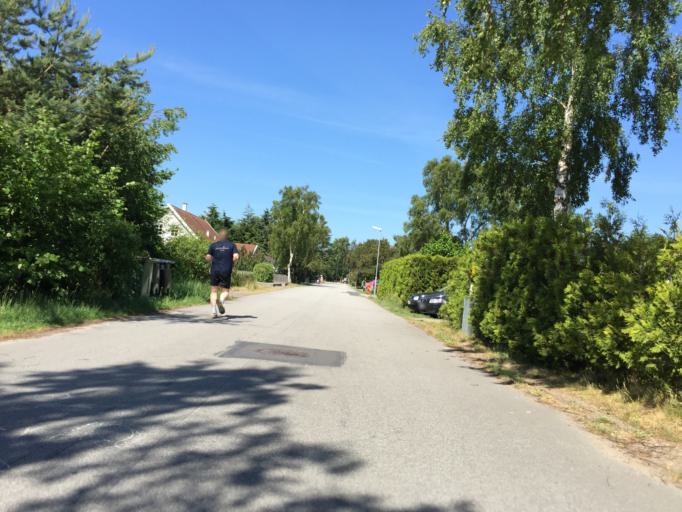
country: SE
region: Skane
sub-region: Trelleborgs Kommun
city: Anderslov
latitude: 55.3491
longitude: 13.2657
